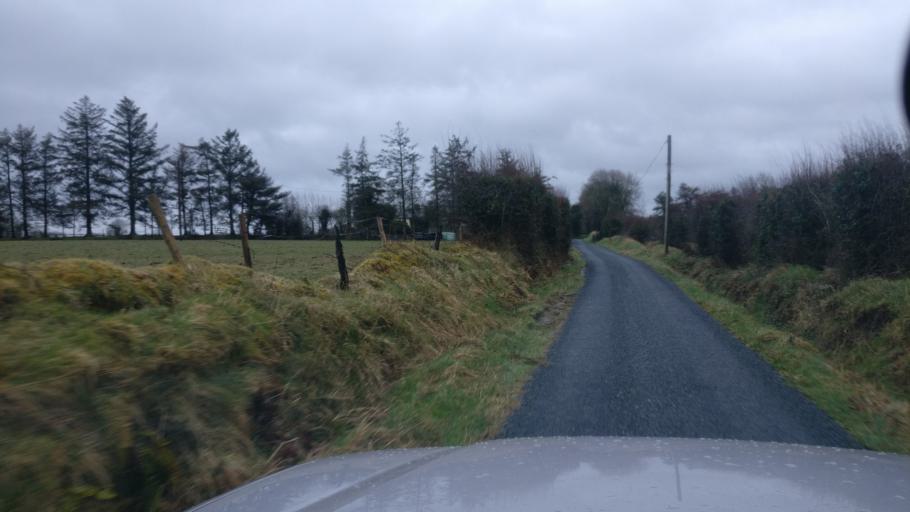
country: IE
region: Connaught
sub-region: County Galway
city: Ballinasloe
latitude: 53.2520
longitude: -8.3575
